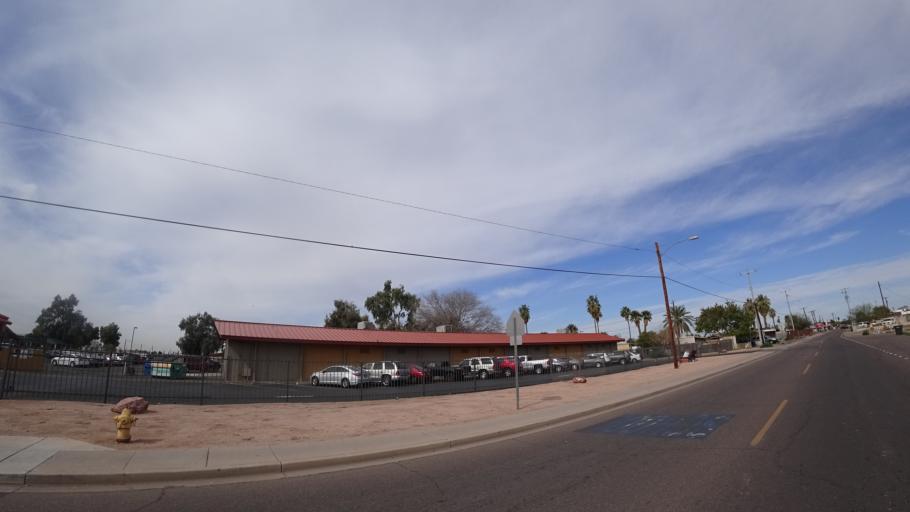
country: US
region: Arizona
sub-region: Maricopa County
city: Phoenix
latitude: 33.4488
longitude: -112.1260
